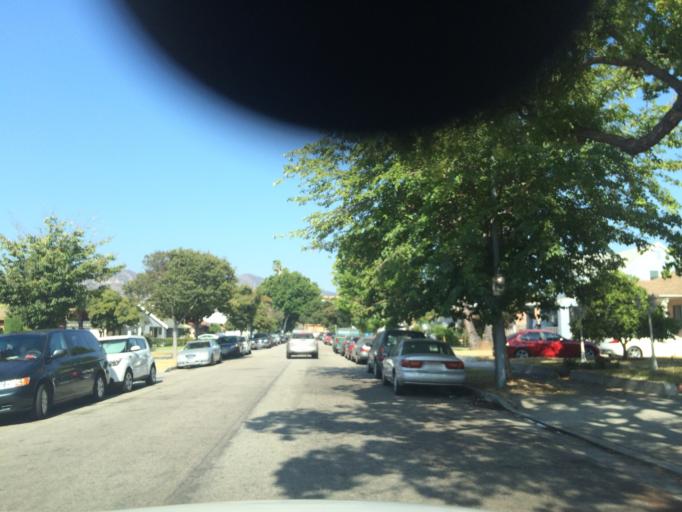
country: US
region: California
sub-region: Los Angeles County
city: Glendale
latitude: 34.1376
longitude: -118.2620
